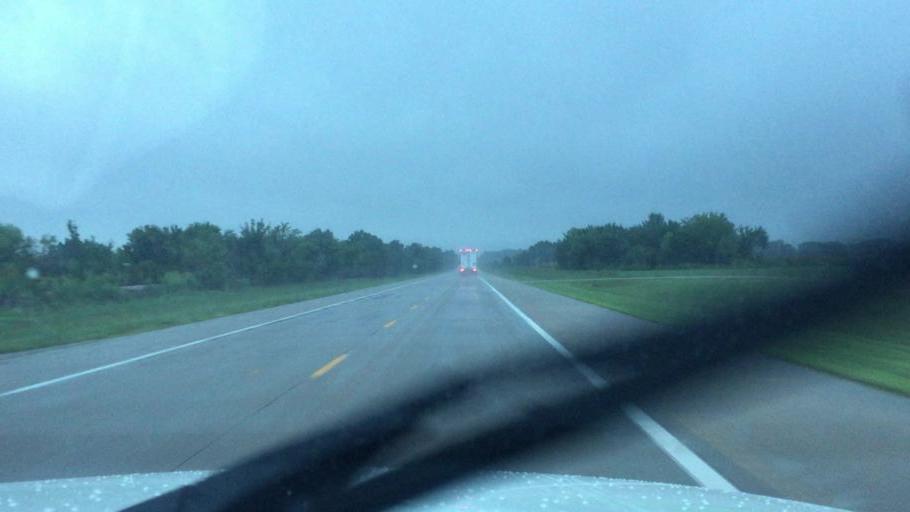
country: US
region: Kansas
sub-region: Neosho County
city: Chanute
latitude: 37.5620
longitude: -95.4709
